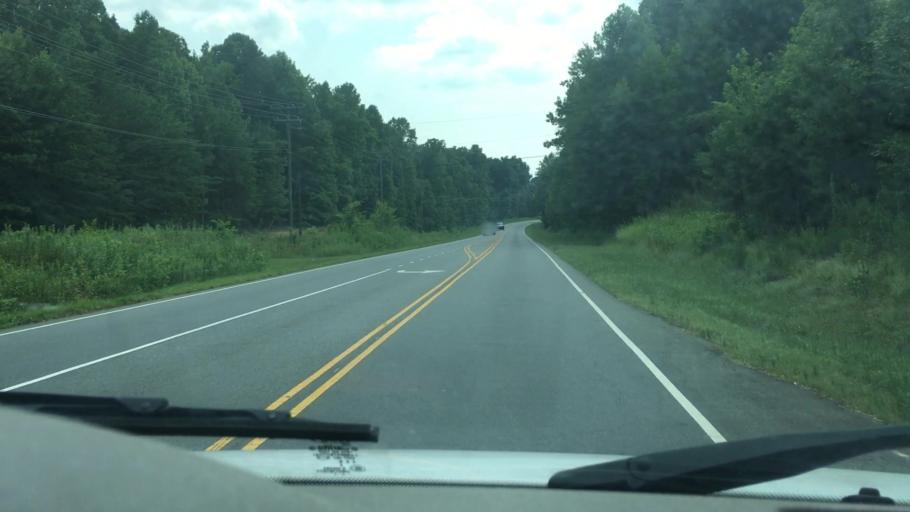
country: US
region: North Carolina
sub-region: Mecklenburg County
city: Huntersville
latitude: 35.4440
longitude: -80.8371
